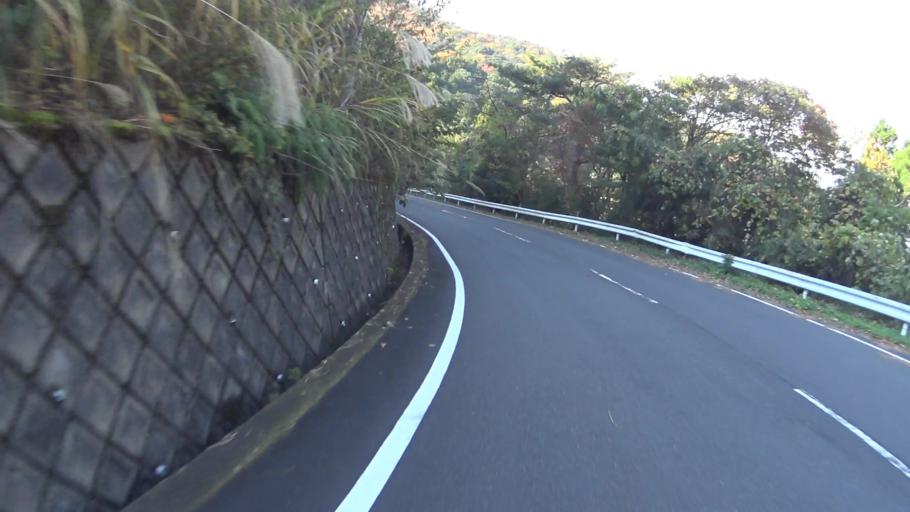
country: JP
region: Kyoto
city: Maizuru
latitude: 35.5481
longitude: 135.3959
